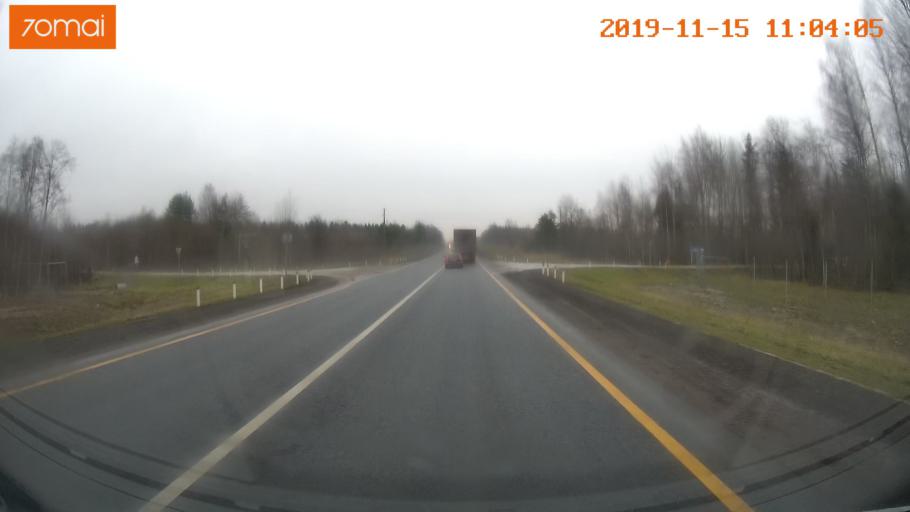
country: RU
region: Vologda
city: Chebsara
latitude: 59.1218
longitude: 38.9757
